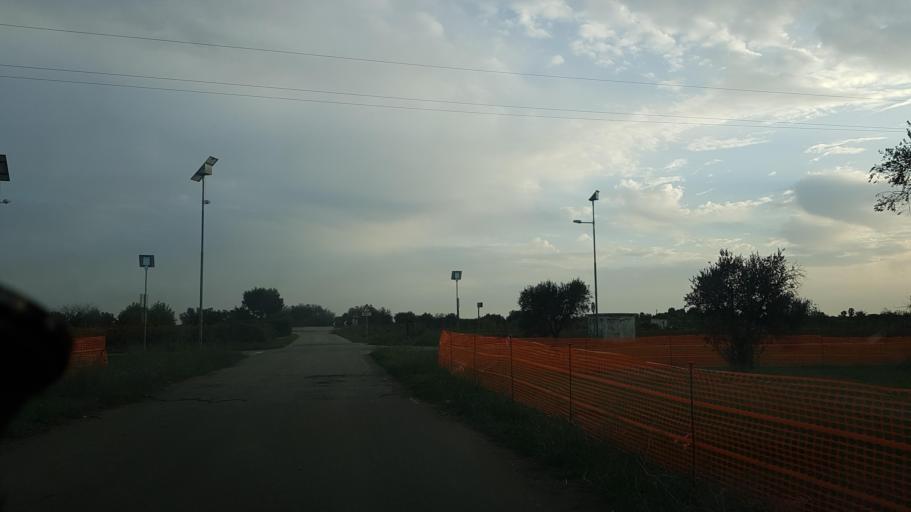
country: IT
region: Apulia
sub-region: Provincia di Brindisi
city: San Pancrazio Salentino
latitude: 40.4085
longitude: 17.8431
